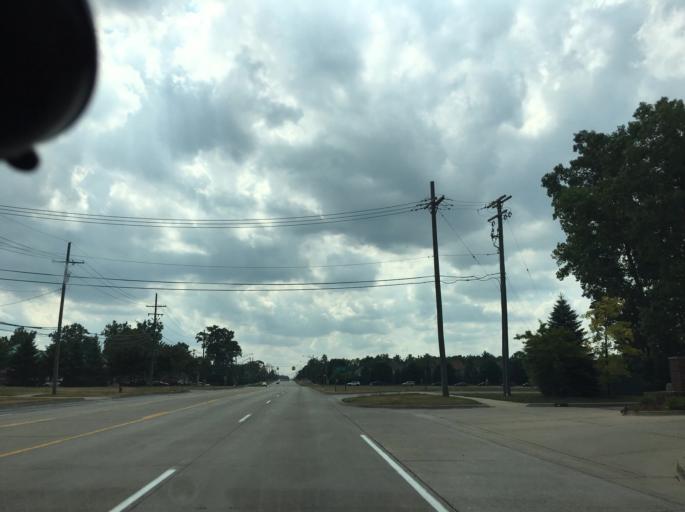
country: US
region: Michigan
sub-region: Macomb County
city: Fraser
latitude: 42.5532
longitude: -82.9677
